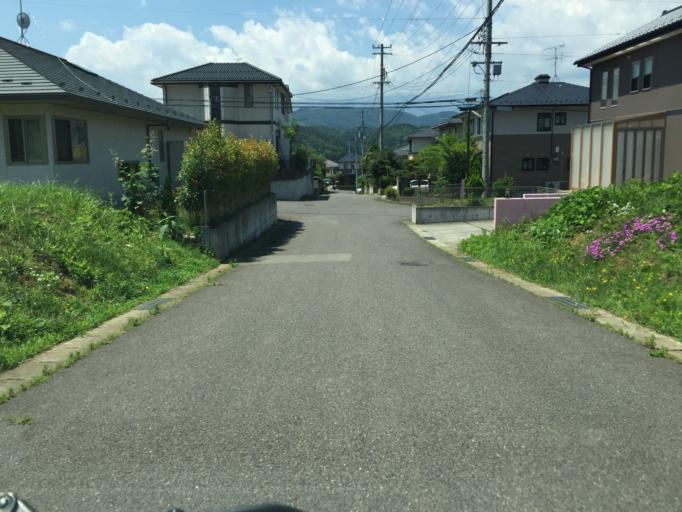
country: JP
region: Fukushima
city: Fukushima-shi
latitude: 37.7225
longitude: 140.4097
